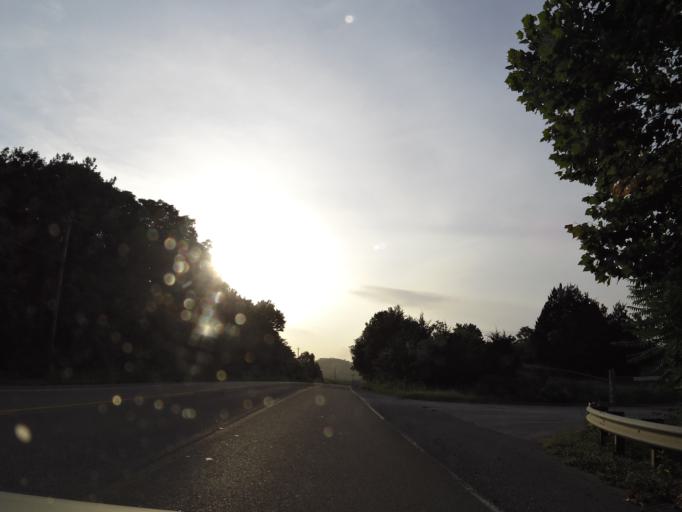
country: US
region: Tennessee
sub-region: Knox County
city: Knoxville
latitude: 35.9551
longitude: -83.8140
